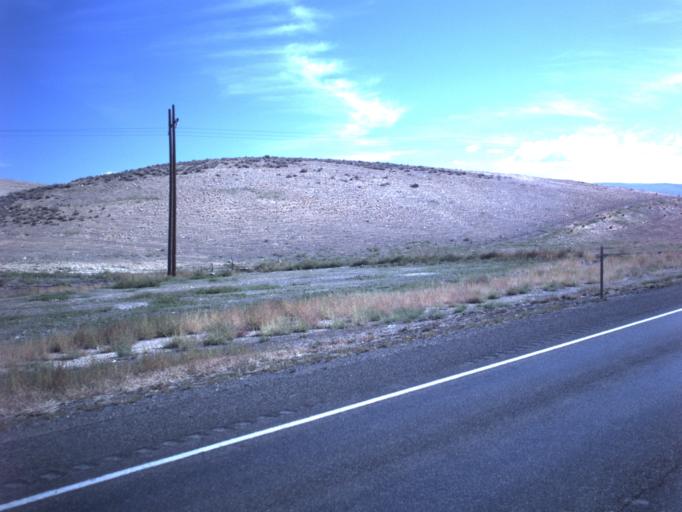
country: US
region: Utah
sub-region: Sanpete County
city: Gunnison
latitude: 39.1719
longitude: -111.8315
